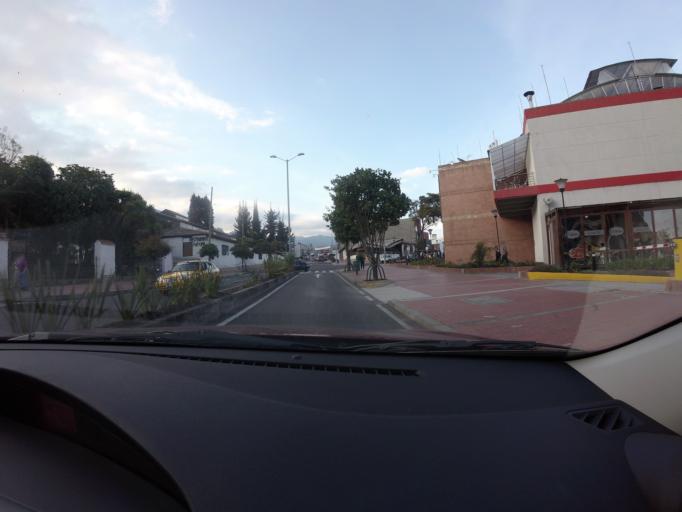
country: CO
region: Cundinamarca
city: Zipaquira
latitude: 5.0183
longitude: -74.0048
